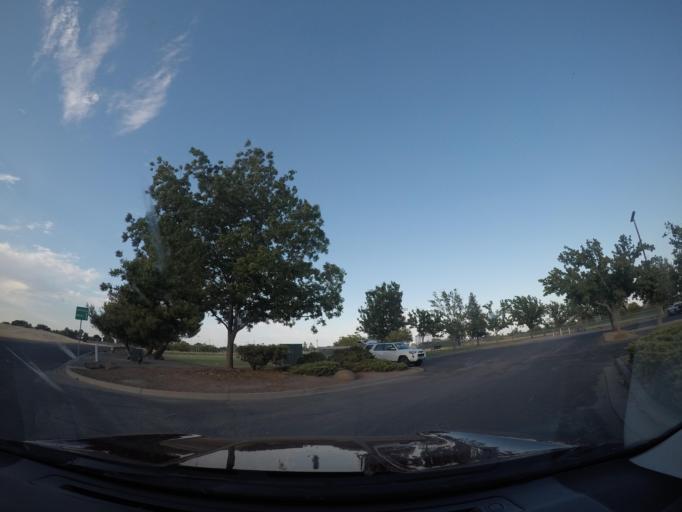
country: US
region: California
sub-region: Solano County
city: Vacaville
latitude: 38.3726
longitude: -121.9741
